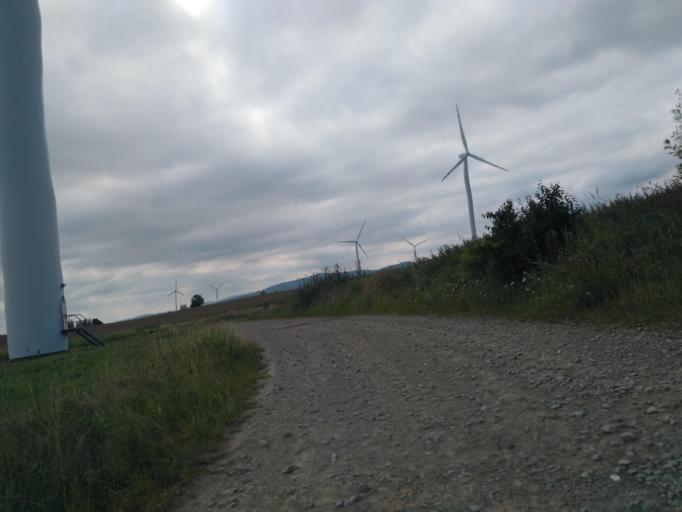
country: PL
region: Subcarpathian Voivodeship
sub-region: Powiat krosnienski
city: Rymanow
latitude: 49.6108
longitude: 21.8436
